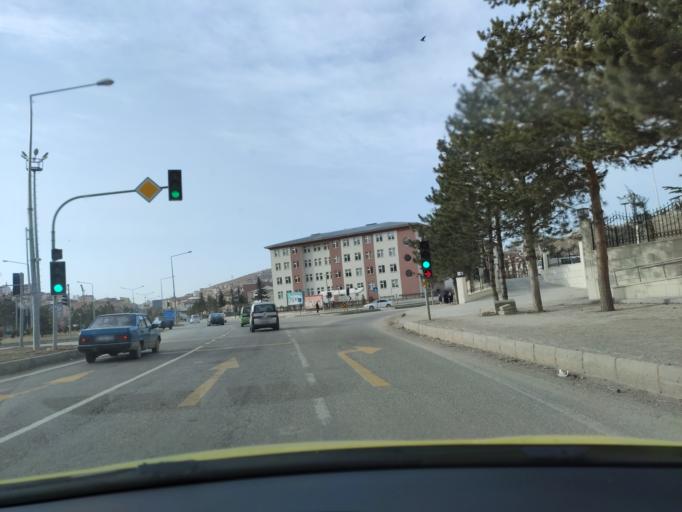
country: TR
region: Bayburt
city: Bayburt
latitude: 40.2487
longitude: 40.2322
